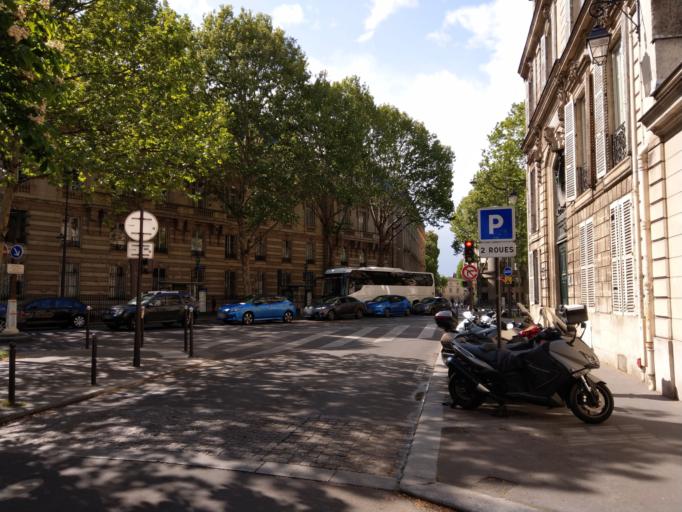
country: FR
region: Ile-de-France
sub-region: Paris
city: Paris
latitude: 48.8597
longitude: 2.3223
